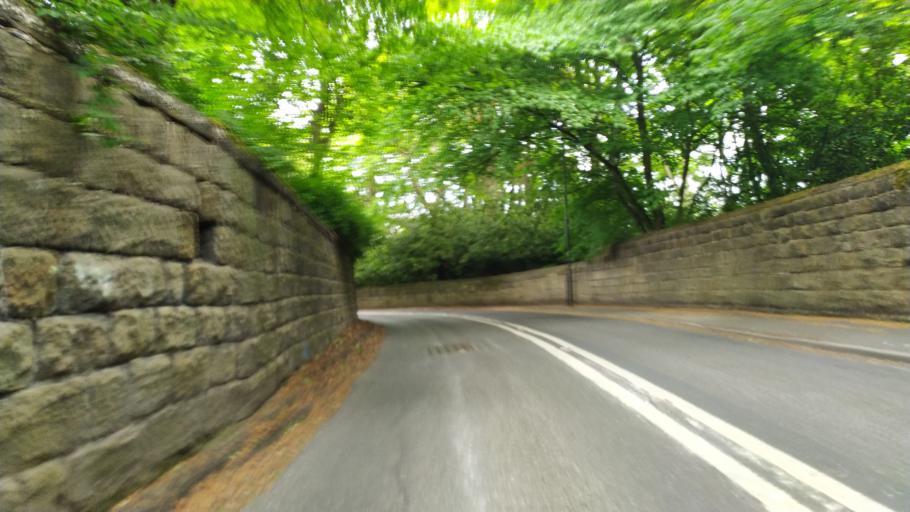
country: GB
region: England
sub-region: City and Borough of Leeds
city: Chapel Allerton
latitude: 53.8354
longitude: -1.5830
